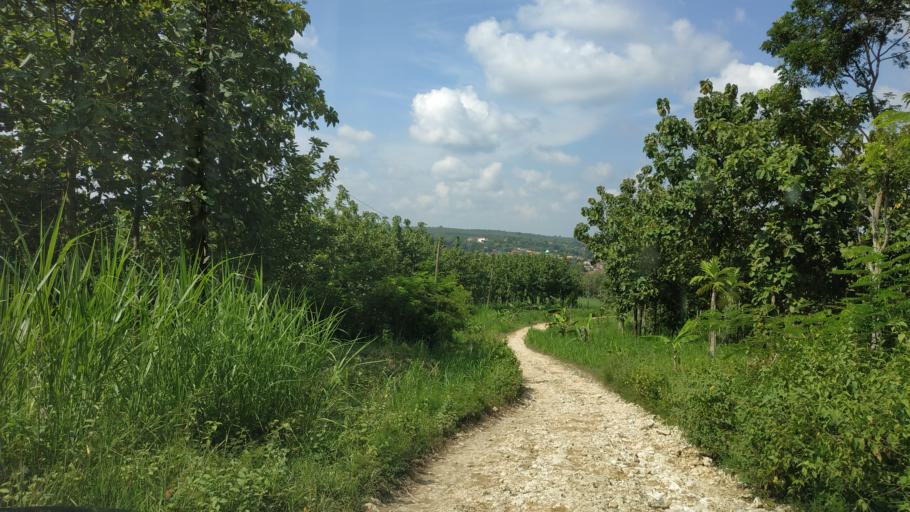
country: ID
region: Central Java
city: Guyangan
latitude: -7.0067
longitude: 111.0990
